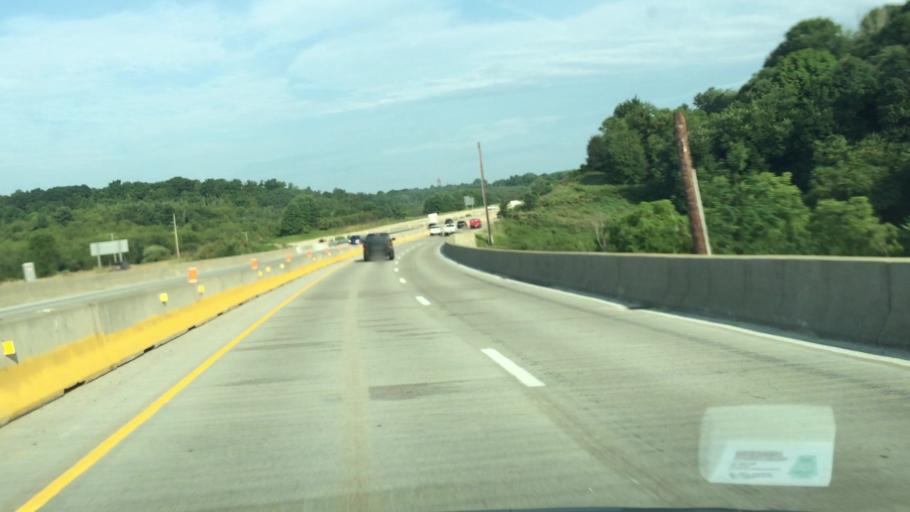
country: US
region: Pennsylvania
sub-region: Allegheny County
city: Enlow
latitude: 40.4689
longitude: -80.2401
